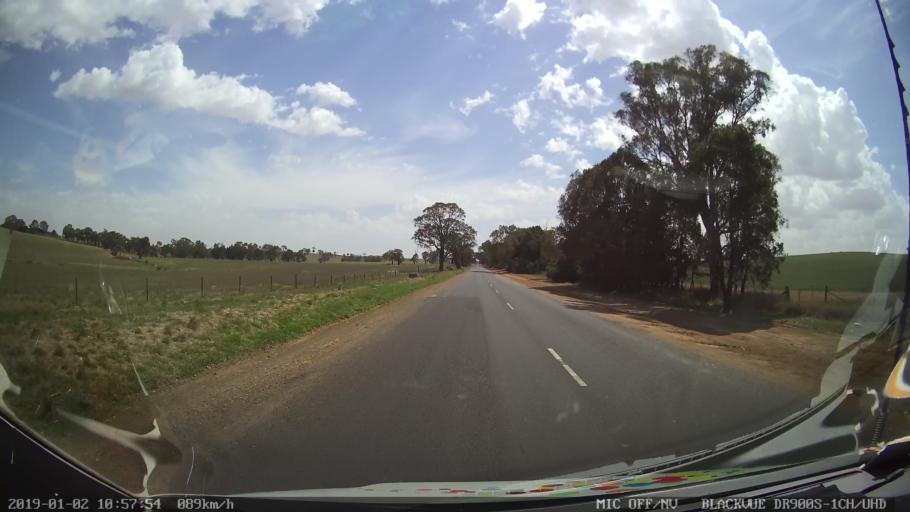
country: AU
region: New South Wales
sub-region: Cootamundra
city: Cootamundra
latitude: -34.6300
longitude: 148.2863
